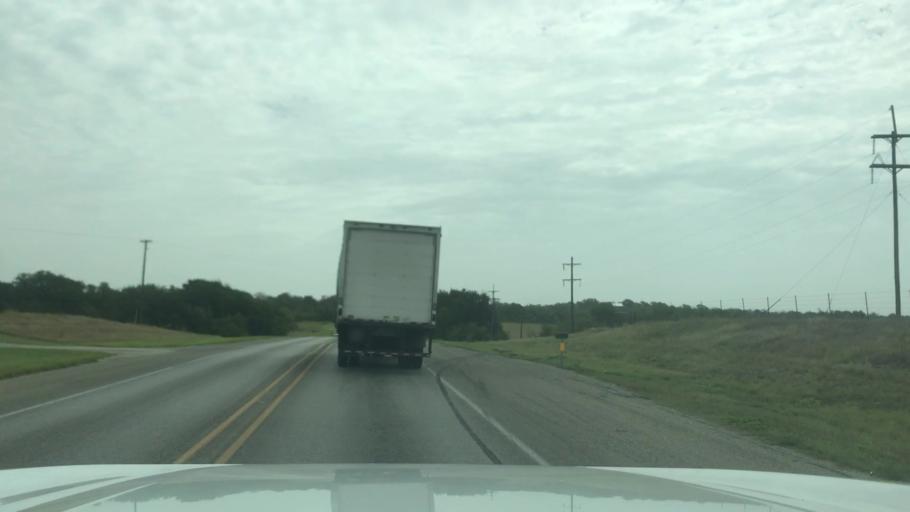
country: US
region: Texas
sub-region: Comanche County
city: De Leon
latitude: 32.0915
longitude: -98.4432
